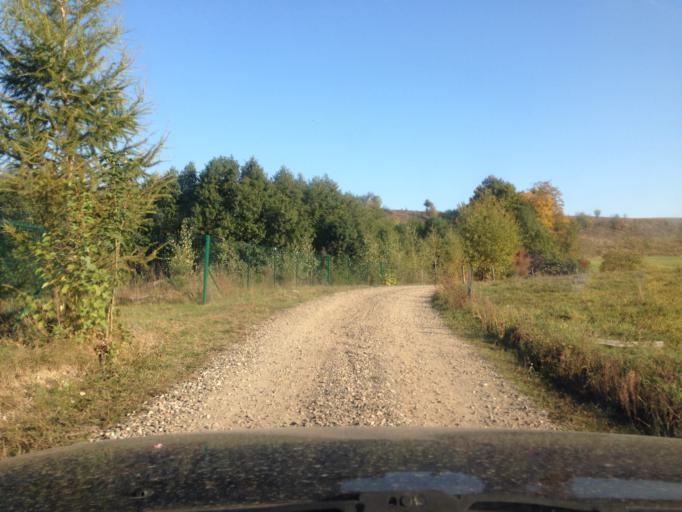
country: PL
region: Kujawsko-Pomorskie
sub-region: Powiat brodnicki
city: Gorzno
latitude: 53.2059
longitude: 19.6571
